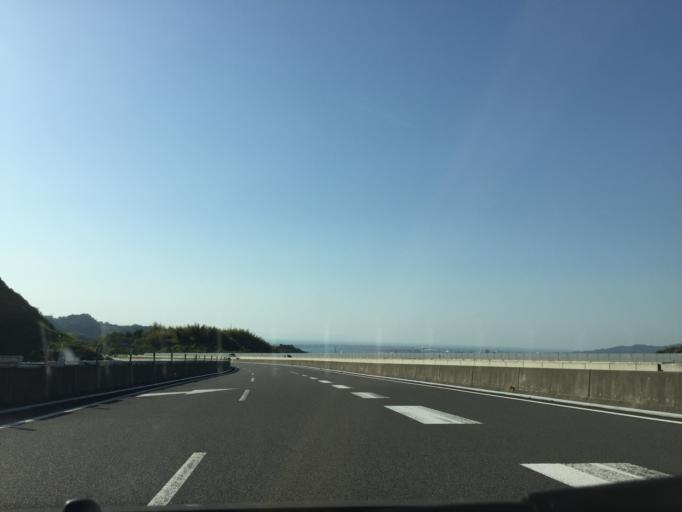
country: JP
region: Shizuoka
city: Shizuoka-shi
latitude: 35.0744
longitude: 138.4667
